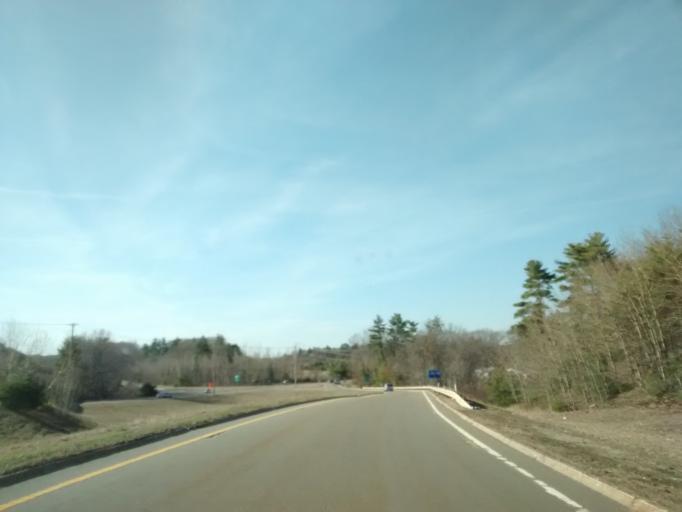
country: US
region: Massachusetts
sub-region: Worcester County
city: East Douglas
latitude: 42.0887
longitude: -71.6939
